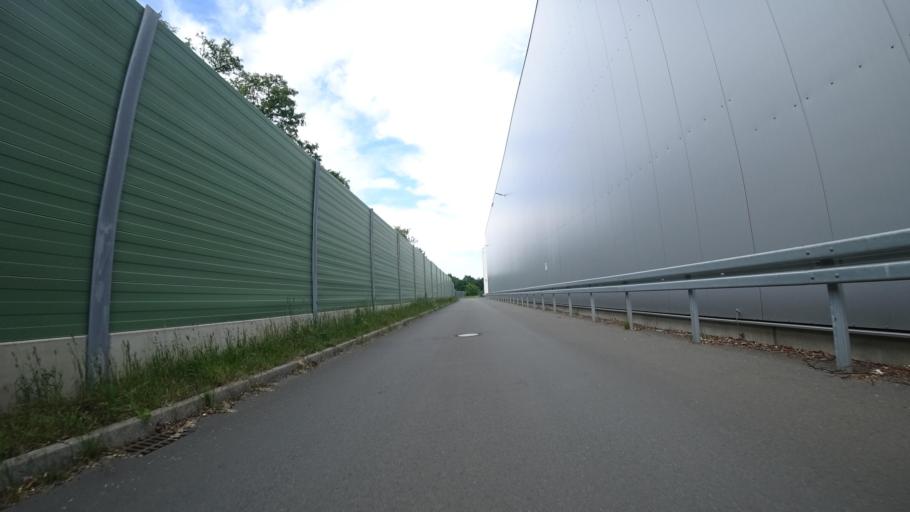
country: DE
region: North Rhine-Westphalia
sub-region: Regierungsbezirk Detmold
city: Guetersloh
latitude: 51.9166
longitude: 8.3982
